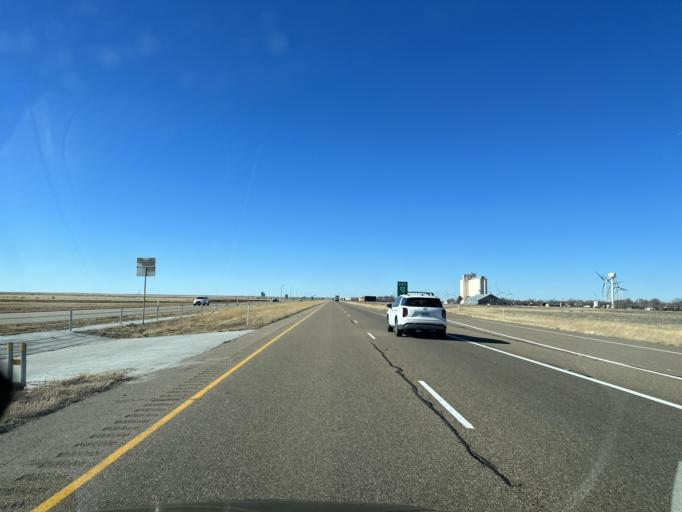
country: US
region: Texas
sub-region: Oldham County
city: Vega
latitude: 35.2701
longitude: -102.6579
